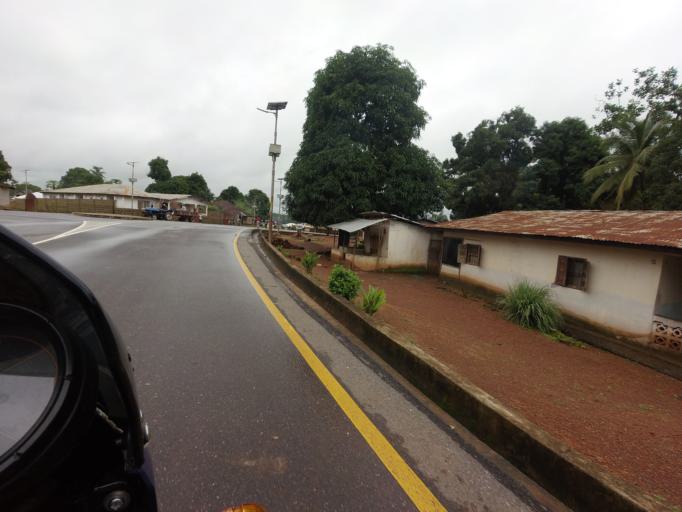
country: SL
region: Northern Province
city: Kambia
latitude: 9.1263
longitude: -12.9180
